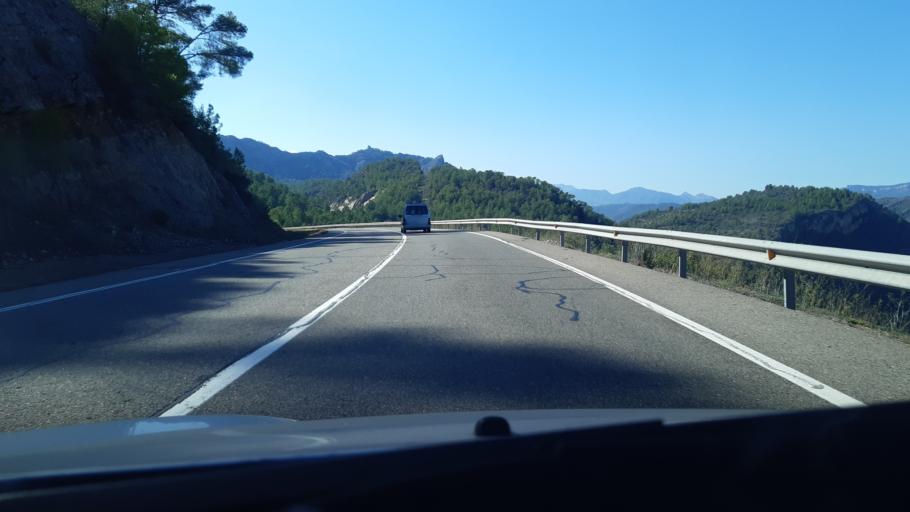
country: ES
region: Catalonia
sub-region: Provincia de Tarragona
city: Rasquera
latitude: 41.0005
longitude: 0.5815
